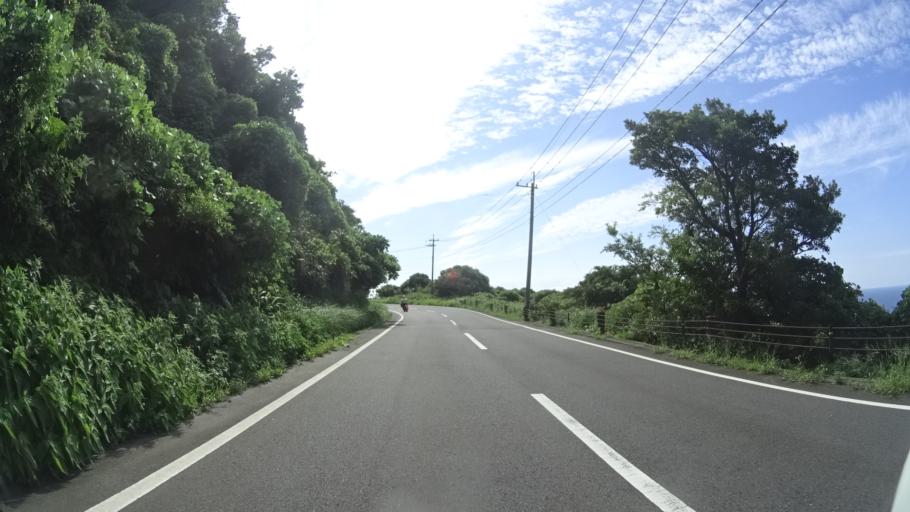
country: JP
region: Kagoshima
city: Nishinoomote
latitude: 30.4300
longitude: 130.4511
